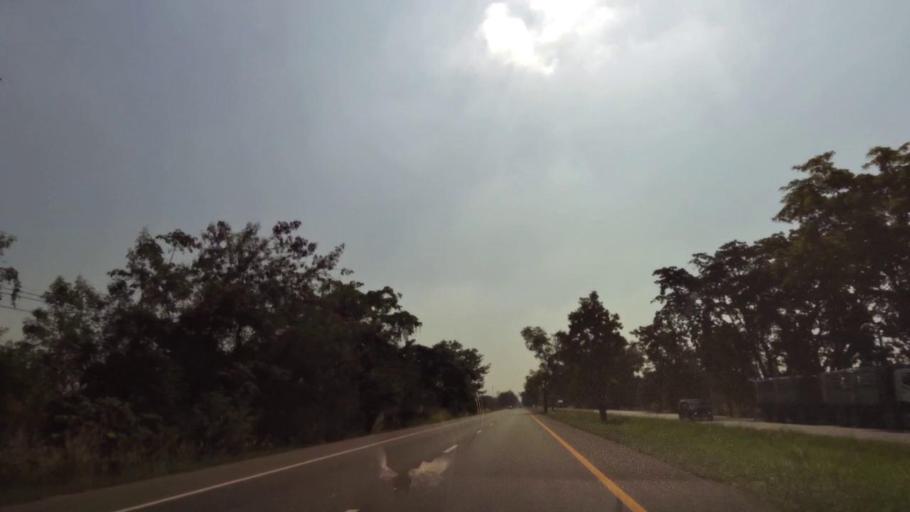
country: TH
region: Phichit
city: Bueng Na Rang
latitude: 16.2075
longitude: 100.1275
